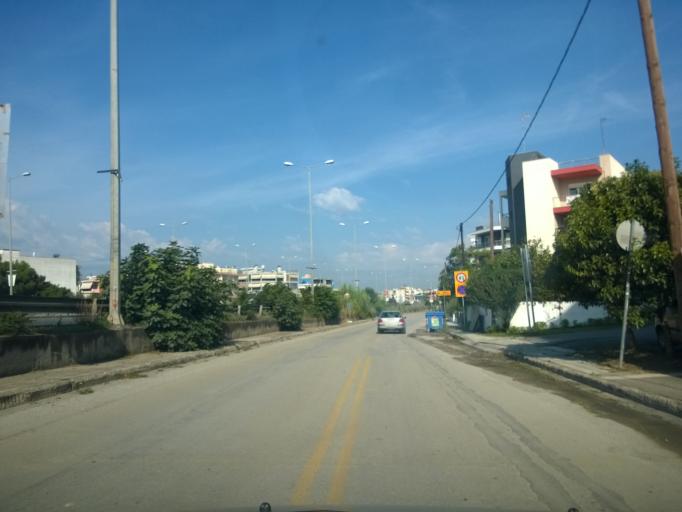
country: GR
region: Central Macedonia
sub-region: Nomos Thessalonikis
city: Kalamaria
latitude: 40.5897
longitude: 22.9681
